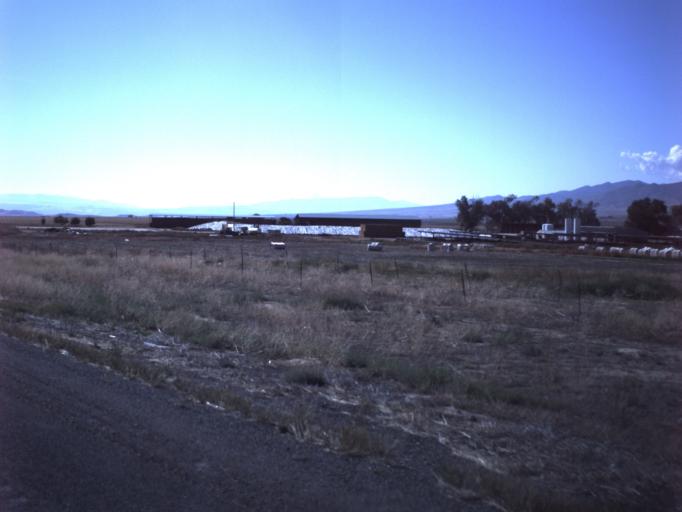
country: US
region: Utah
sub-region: Sanpete County
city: Gunnison
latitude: 39.2654
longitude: -111.8684
